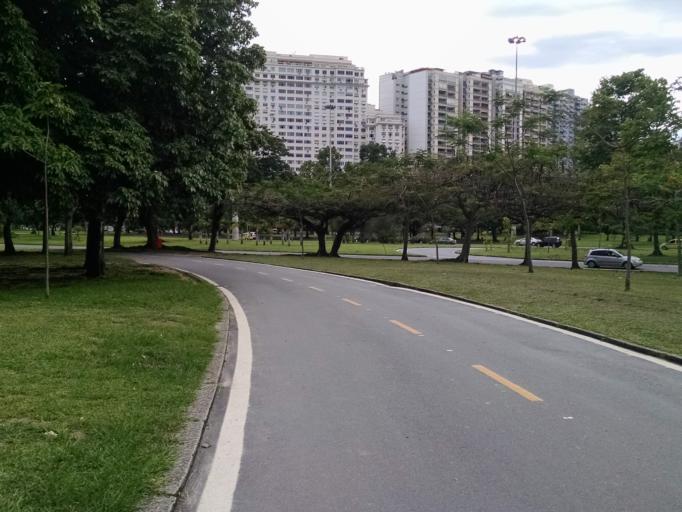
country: BR
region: Rio de Janeiro
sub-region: Rio De Janeiro
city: Rio de Janeiro
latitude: -22.9357
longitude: -43.1723
